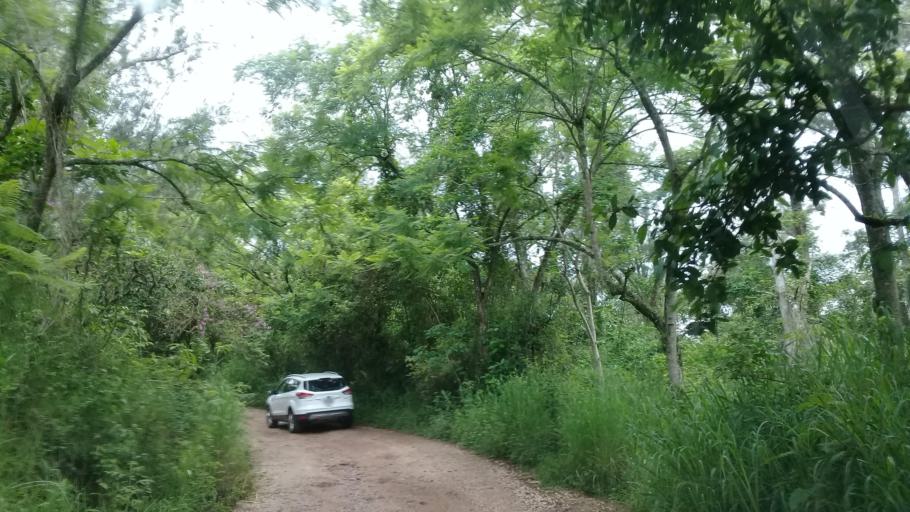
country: MX
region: Veracruz
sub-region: Emiliano Zapata
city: Jacarandas
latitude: 19.5068
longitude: -96.8432
